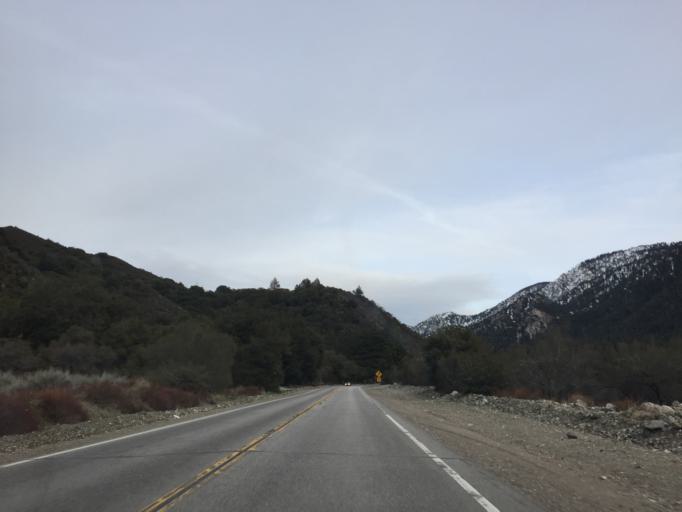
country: US
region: California
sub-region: San Bernardino County
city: Yucaipa
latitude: 34.0950
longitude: -116.9459
